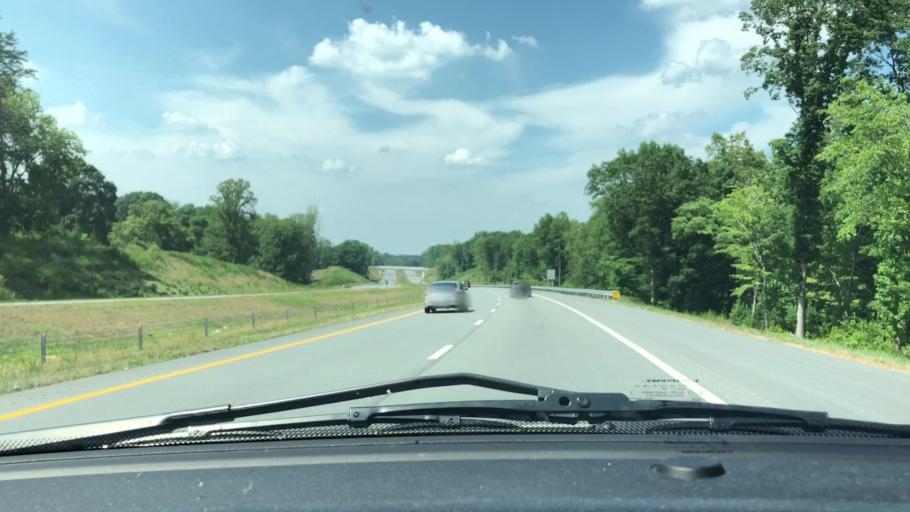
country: US
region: North Carolina
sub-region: Guilford County
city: Oak Ridge
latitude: 36.1443
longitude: -79.9586
